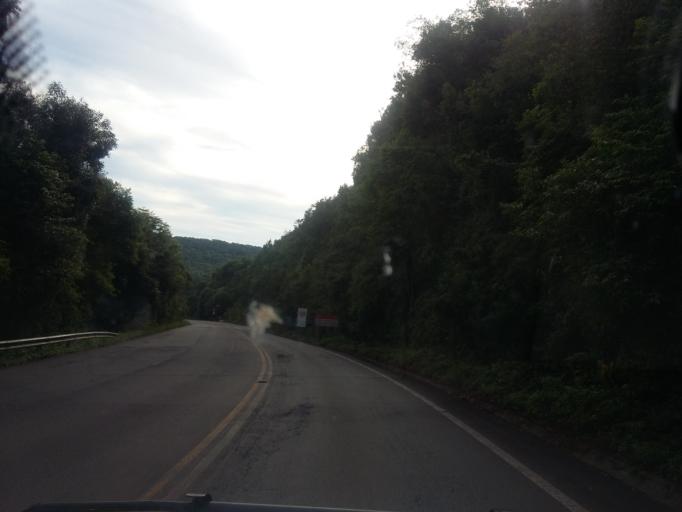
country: BR
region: Santa Catarina
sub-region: Celso Ramos
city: Celso Ramos
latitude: -27.6183
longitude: -51.4840
